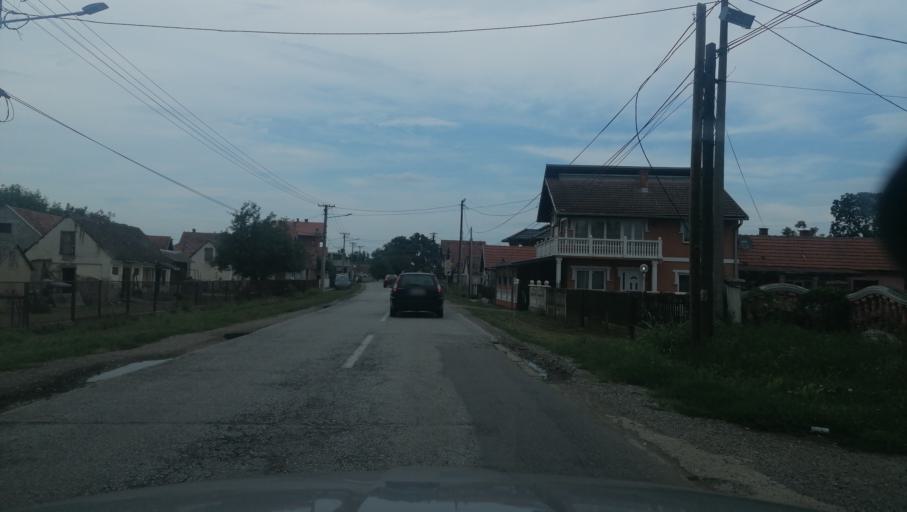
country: RS
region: Central Serbia
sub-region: Macvanski Okrug
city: Bogatic
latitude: 44.8331
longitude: 19.4700
